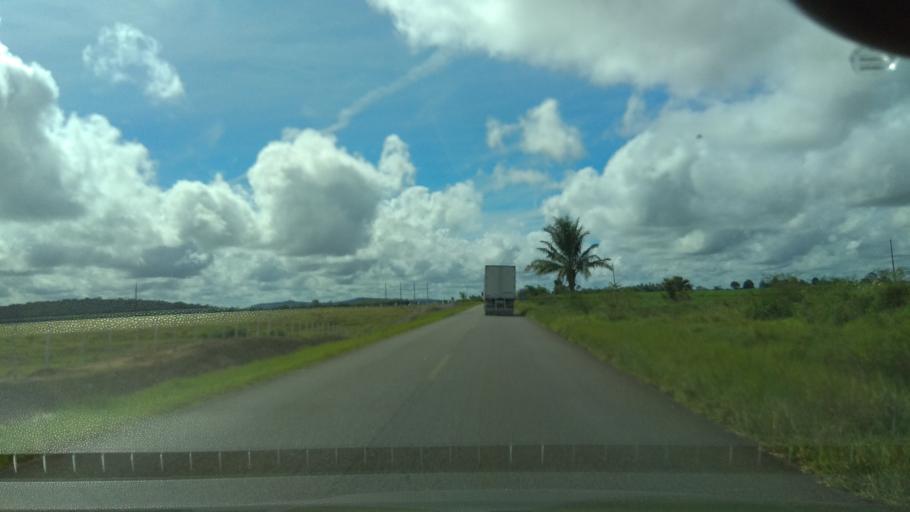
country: BR
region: Bahia
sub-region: Mutuipe
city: Mutuipe
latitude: -13.1696
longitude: -39.3476
